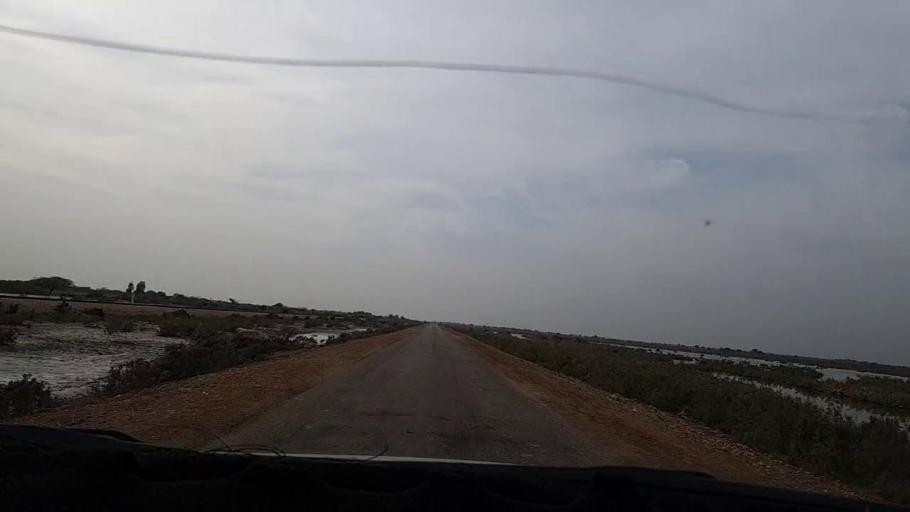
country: PK
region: Sindh
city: Pithoro
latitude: 25.5156
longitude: 69.2937
